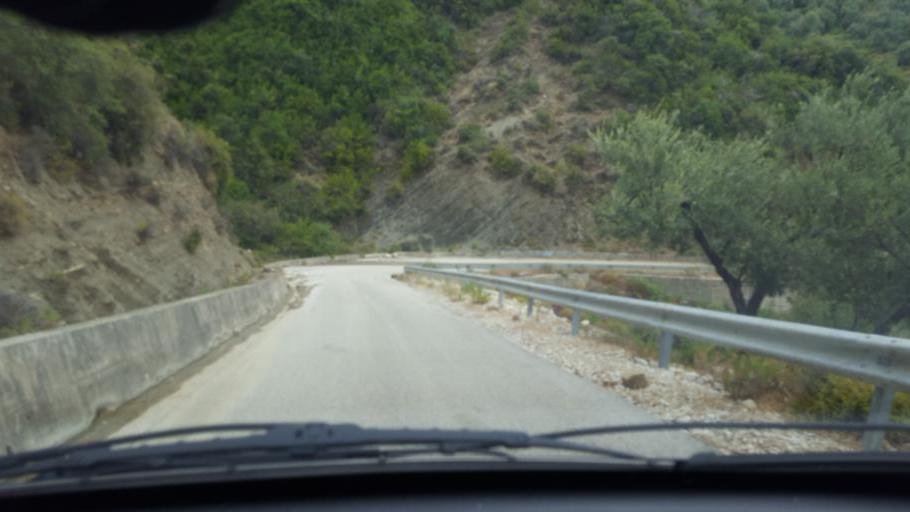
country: AL
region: Vlore
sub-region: Rrethi i Sarandes
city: Lukove
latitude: 39.9858
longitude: 19.9166
